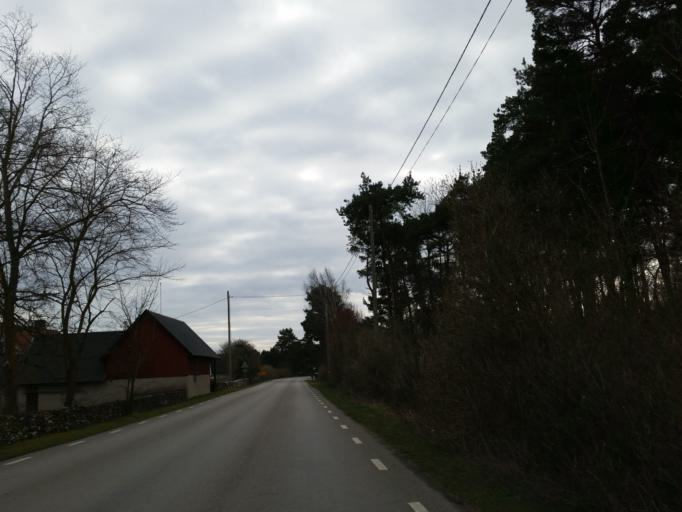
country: SE
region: Kalmar
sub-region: Morbylanga Kommun
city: Sodra Sandby
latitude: 56.5929
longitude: 16.6339
